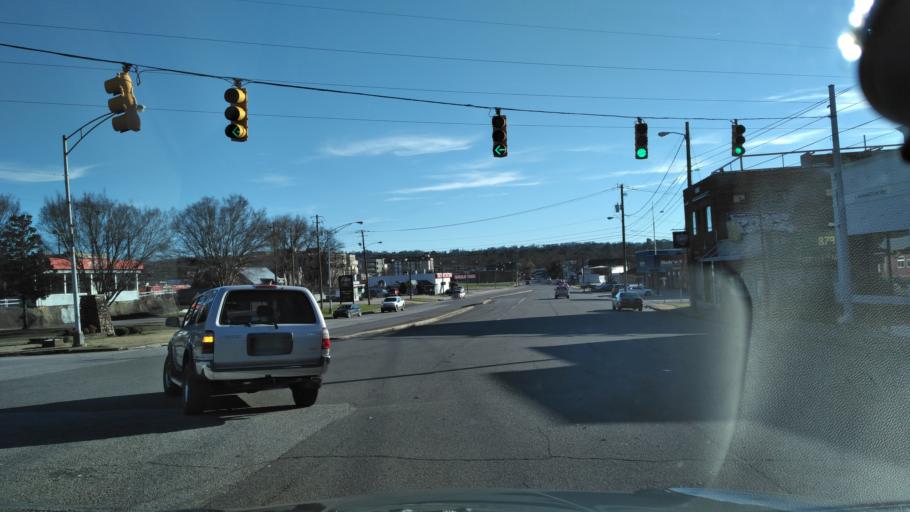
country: US
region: Alabama
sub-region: Jefferson County
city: Homewood
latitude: 33.4843
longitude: -86.7919
